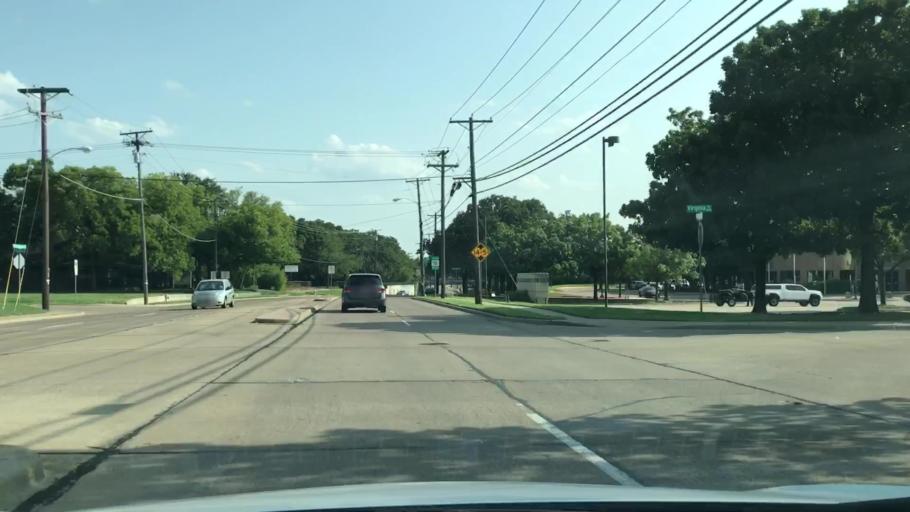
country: US
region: Texas
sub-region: Dallas County
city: Irving
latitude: 32.8173
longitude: -96.9496
